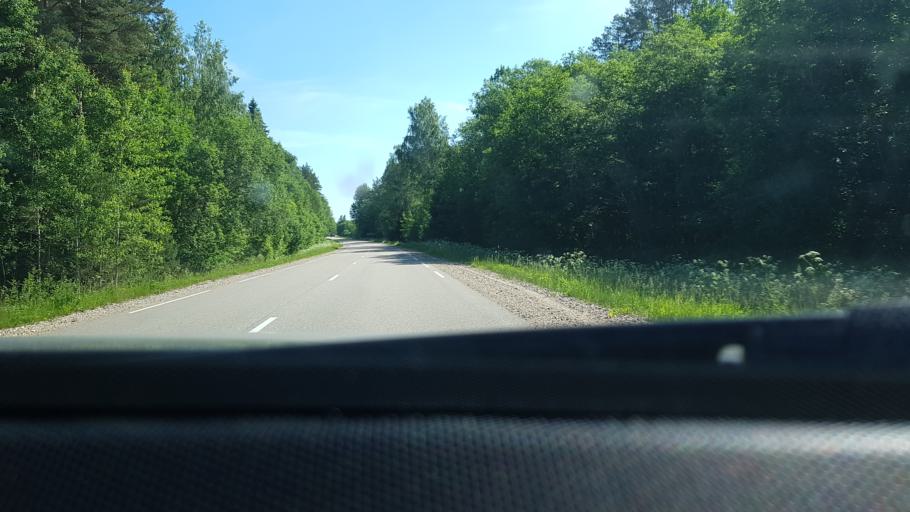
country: BY
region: Vitebsk
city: Braslaw
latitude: 55.8364
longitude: 26.9391
